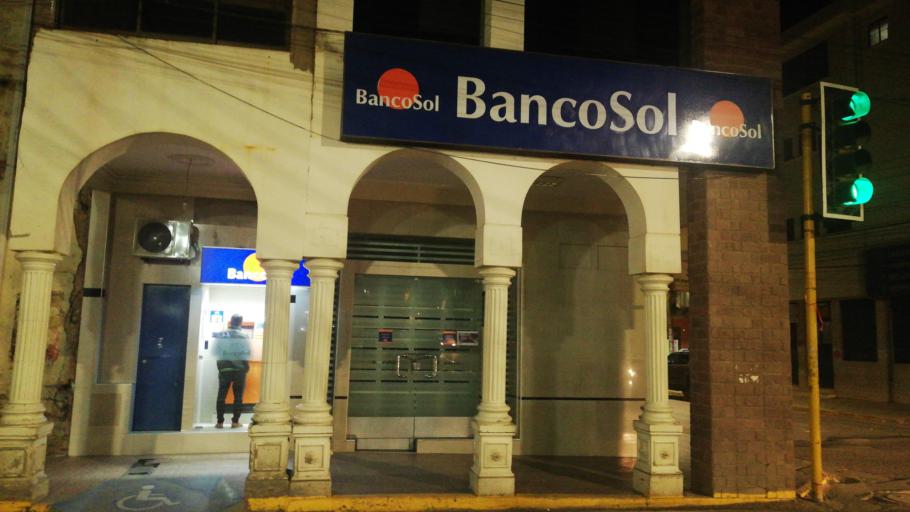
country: BO
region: Cochabamba
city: Cochabamba
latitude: -17.4034
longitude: -66.0403
